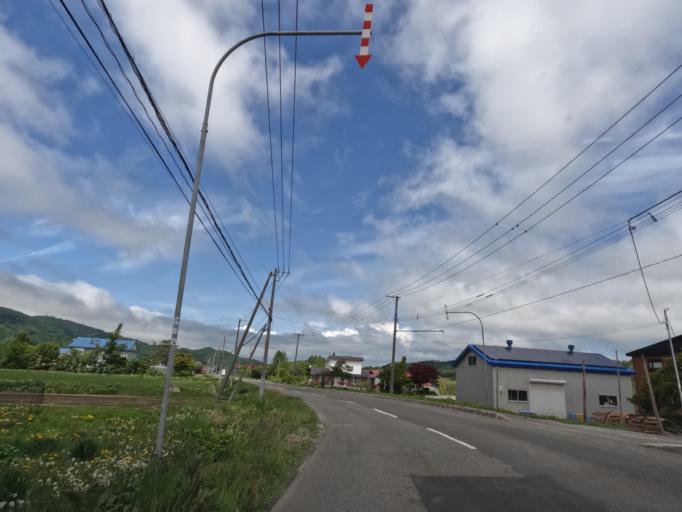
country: JP
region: Hokkaido
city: Tobetsu
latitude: 43.2746
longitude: 141.5338
